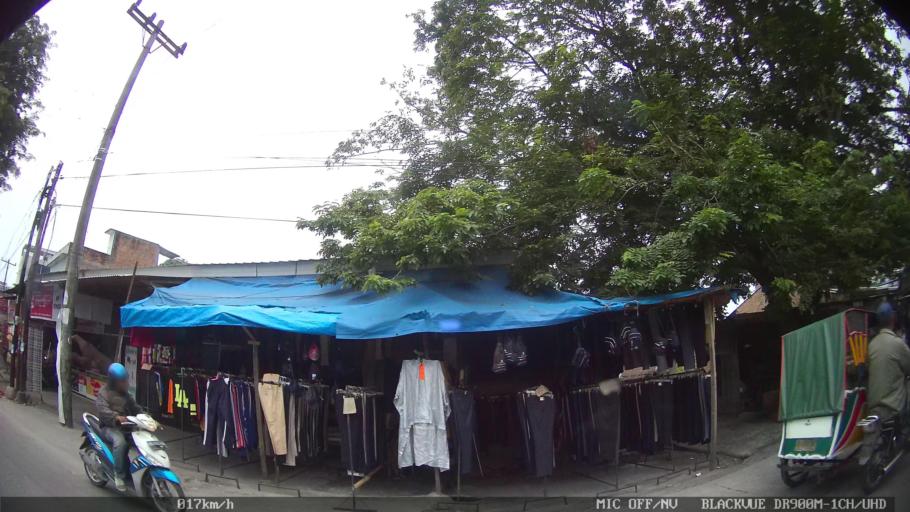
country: ID
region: North Sumatra
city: Medan
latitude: 3.5811
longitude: 98.7285
